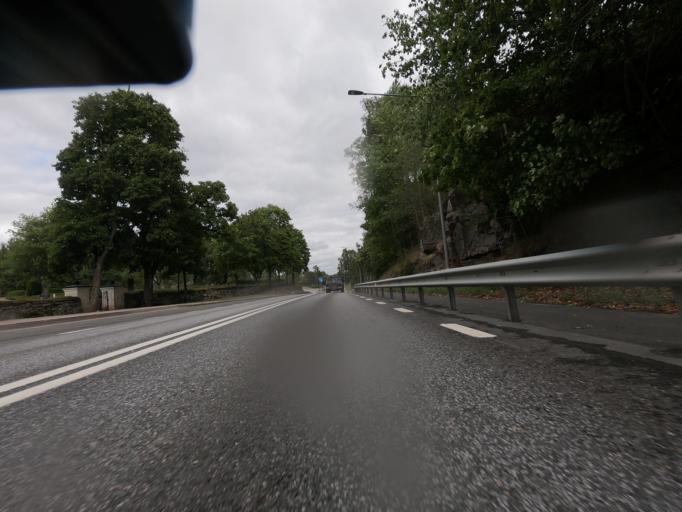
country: SE
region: Joenkoeping
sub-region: Vaggeryds Kommun
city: Vaggeryd
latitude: 57.4709
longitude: 14.3170
